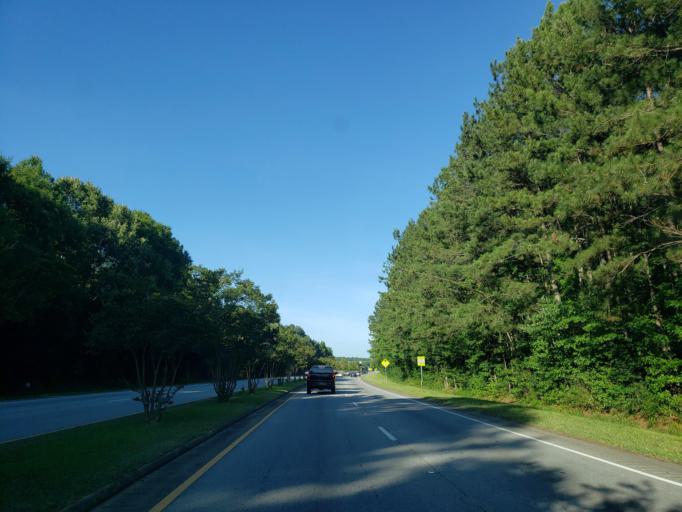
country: US
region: Georgia
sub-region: Floyd County
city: Rome
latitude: 34.2870
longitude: -85.1583
